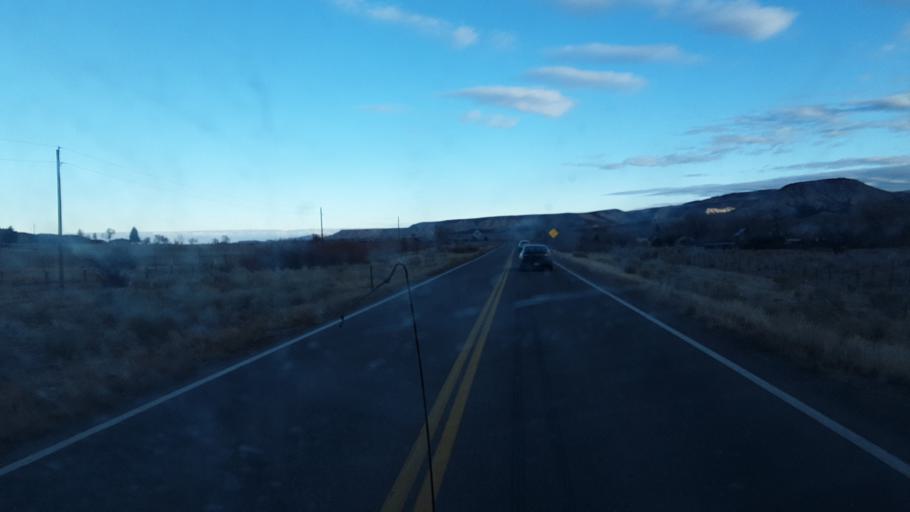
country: US
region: Colorado
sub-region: Montrose County
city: Montrose
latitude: 38.3031
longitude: -107.7733
